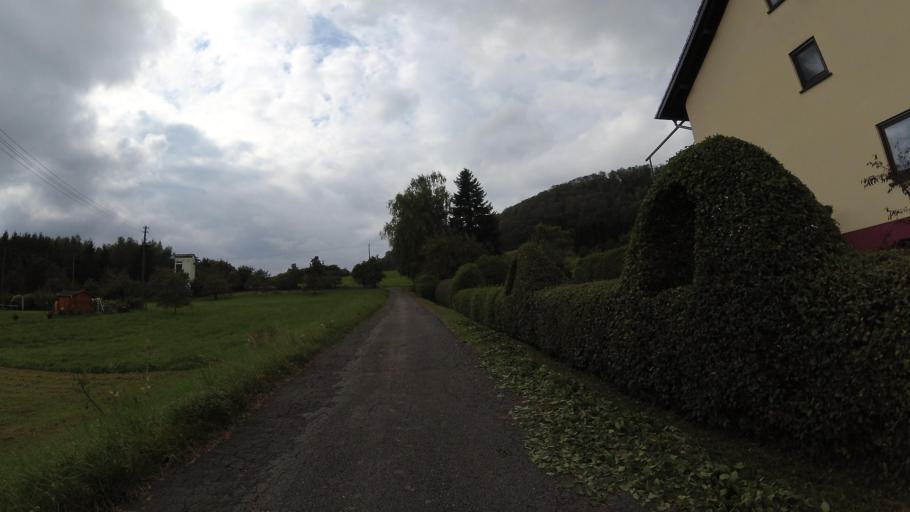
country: DE
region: Rheinland-Pfalz
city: Reichweiler
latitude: 49.5428
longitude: 7.2872
